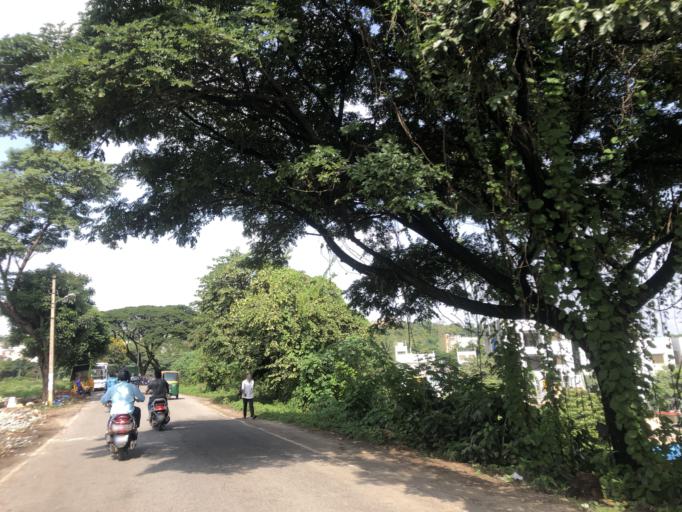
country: IN
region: Karnataka
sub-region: Bangalore Urban
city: Bangalore
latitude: 12.9286
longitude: 77.5340
